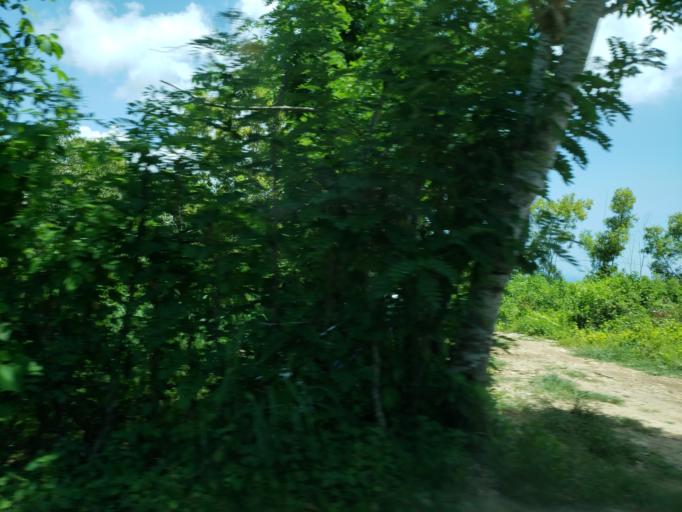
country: ID
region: Bali
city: Kangin
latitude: -8.8346
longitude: 115.1365
